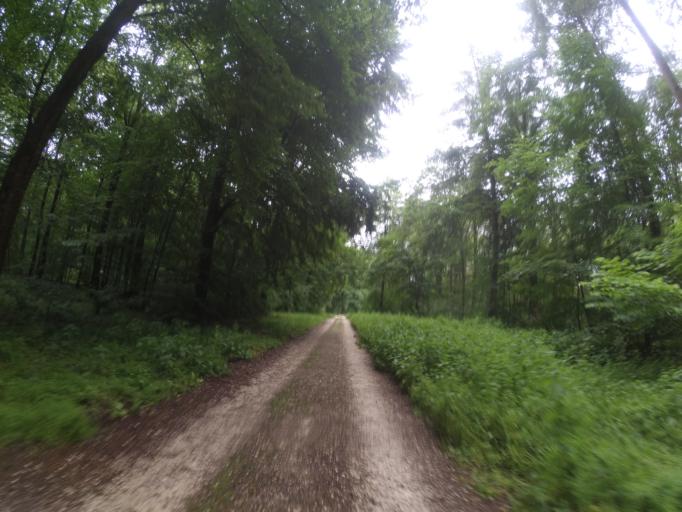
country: DE
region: Baden-Wuerttemberg
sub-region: Tuebingen Region
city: Borslingen
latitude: 48.5108
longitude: 10.0686
